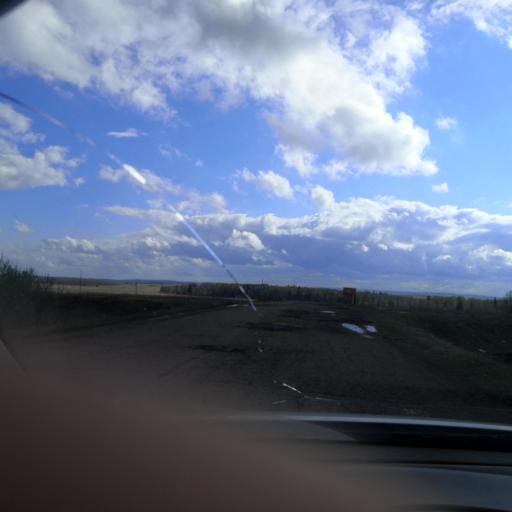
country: RU
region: Bashkortostan
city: Pavlovka
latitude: 55.3223
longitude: 56.3504
